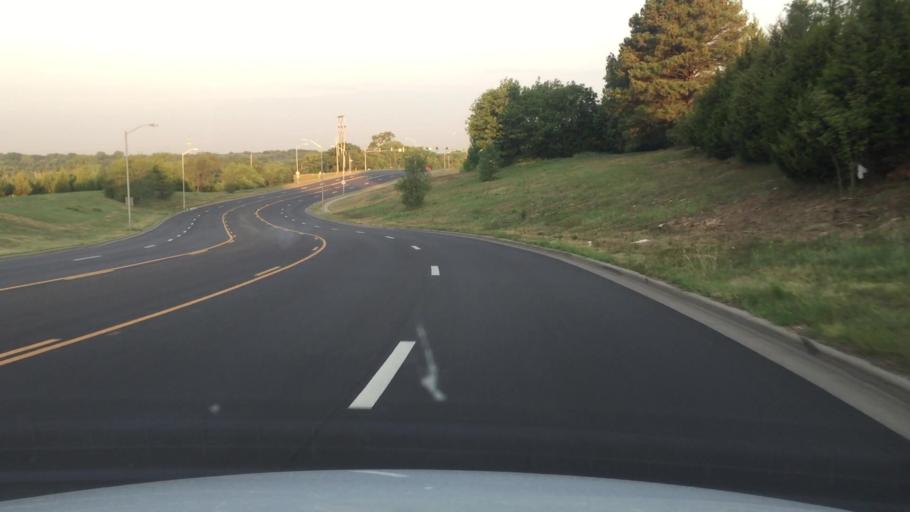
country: US
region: Kansas
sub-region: Wyandotte County
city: Edwardsville
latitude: 39.0225
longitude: -94.7768
